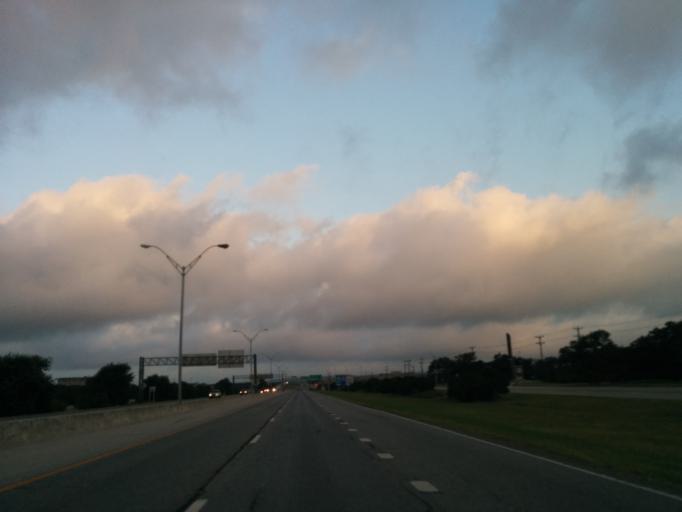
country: US
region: Texas
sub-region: Bexar County
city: Shavano Park
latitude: 29.5895
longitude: -98.6109
